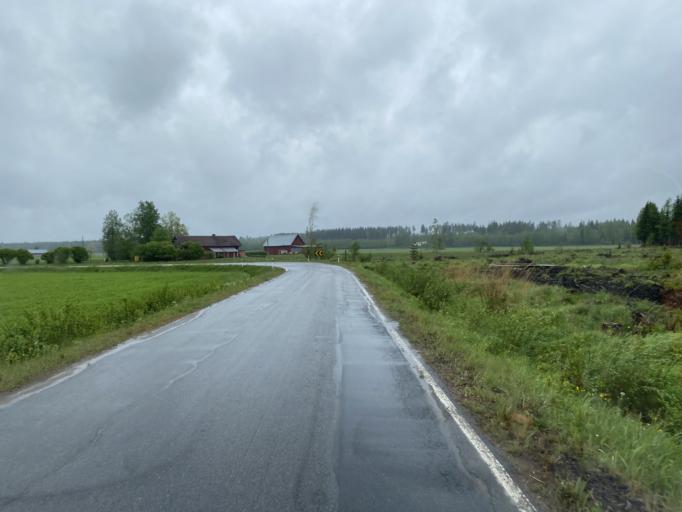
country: FI
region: Haeme
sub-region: Forssa
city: Humppila
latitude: 61.0558
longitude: 23.3260
